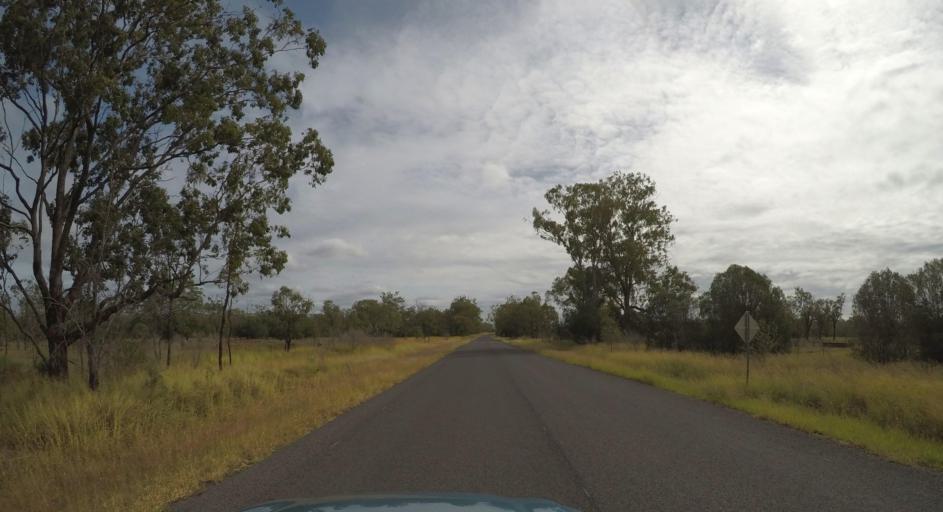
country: AU
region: Queensland
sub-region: Western Downs
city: Dalby
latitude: -27.0522
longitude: 151.3157
